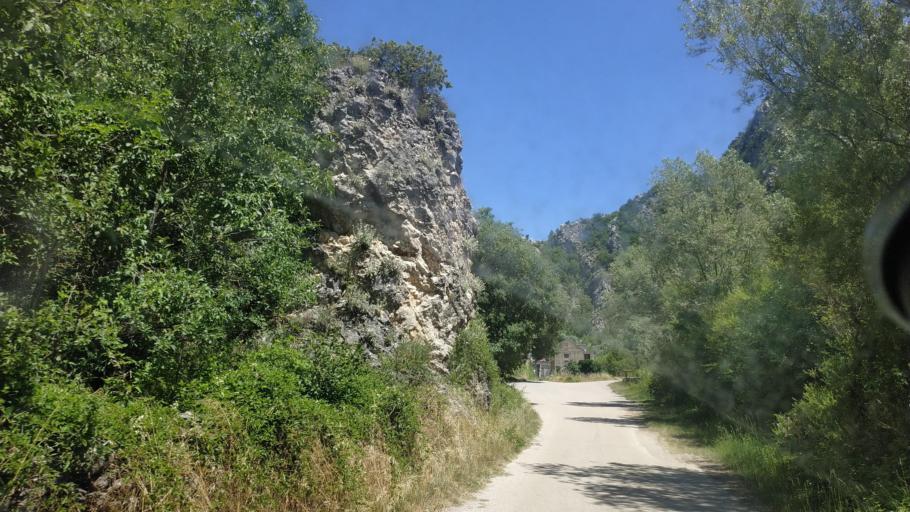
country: HR
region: Sibensko-Kniniska
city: Knin
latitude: 44.0414
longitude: 16.2316
